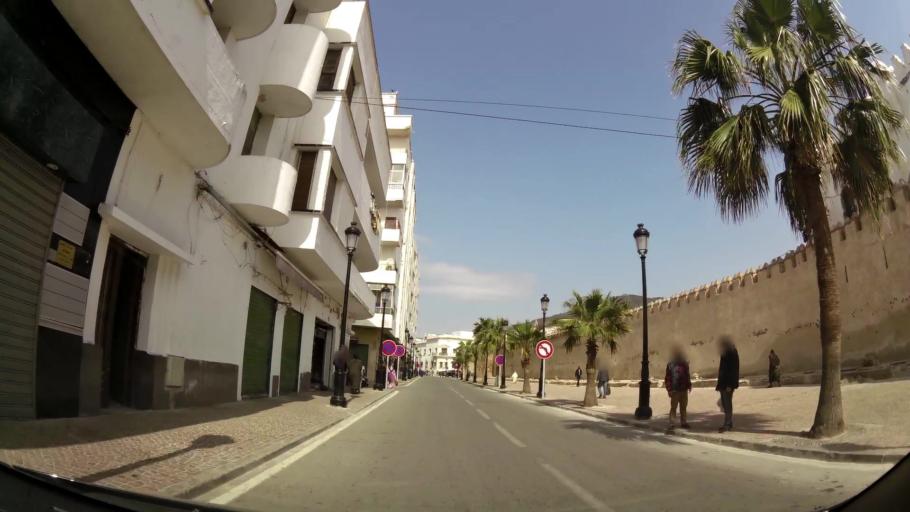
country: MA
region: Tanger-Tetouan
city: Tetouan
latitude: 35.5717
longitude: -5.3744
